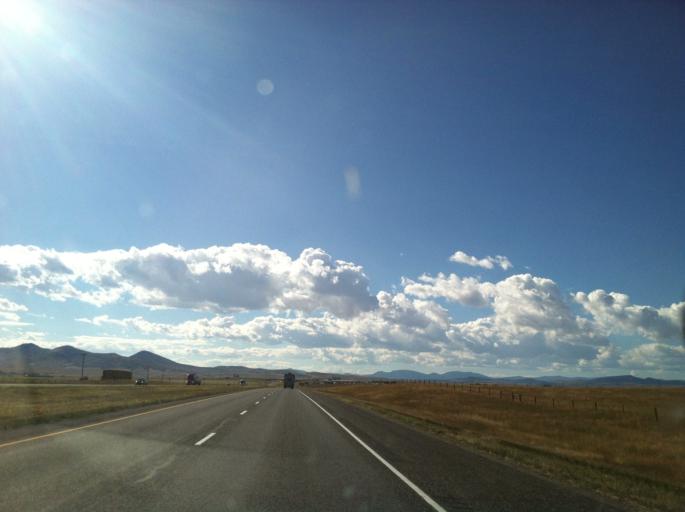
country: US
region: Montana
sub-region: Gallatin County
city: Three Forks
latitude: 45.9186
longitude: -111.5716
